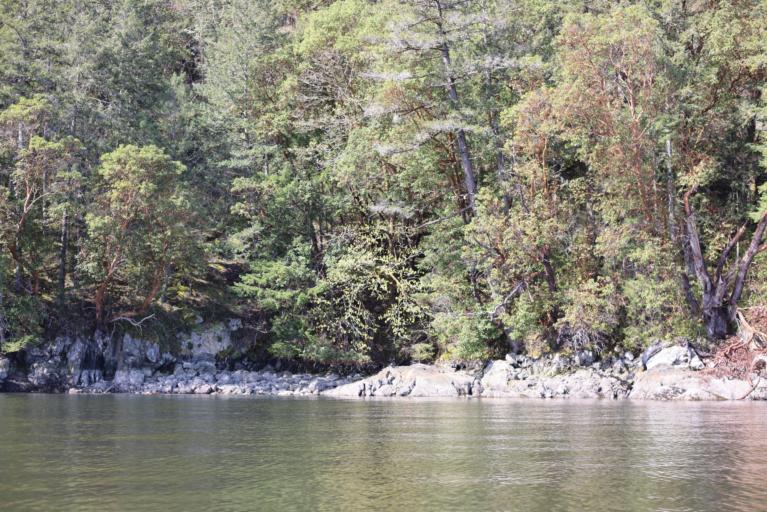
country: CA
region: British Columbia
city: Langford
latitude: 48.5695
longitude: -123.5140
